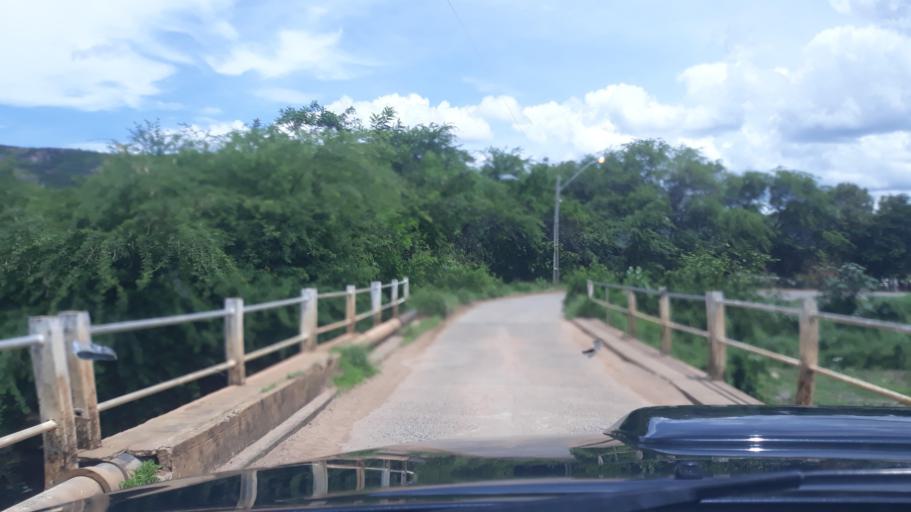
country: BR
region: Bahia
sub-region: Guanambi
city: Guanambi
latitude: -14.2919
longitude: -42.6967
